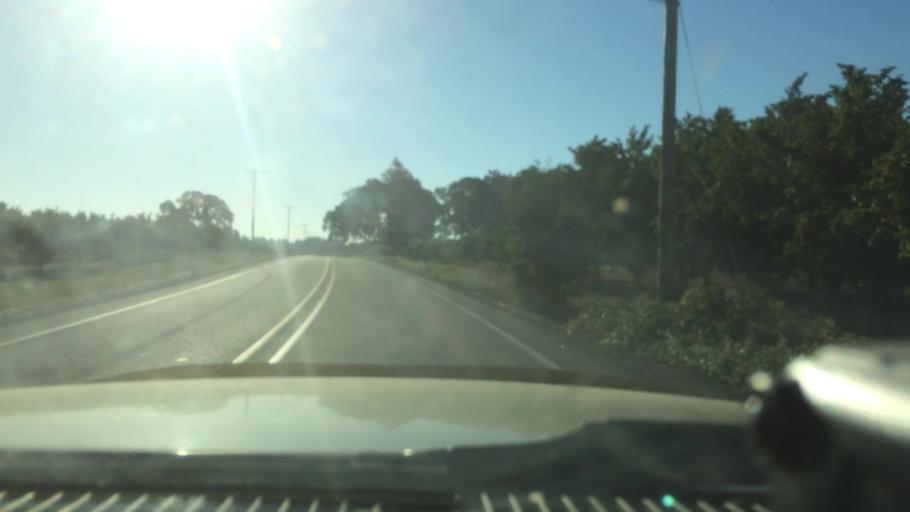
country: US
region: Oregon
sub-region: Marion County
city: Gervais
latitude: 45.1156
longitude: -122.9751
